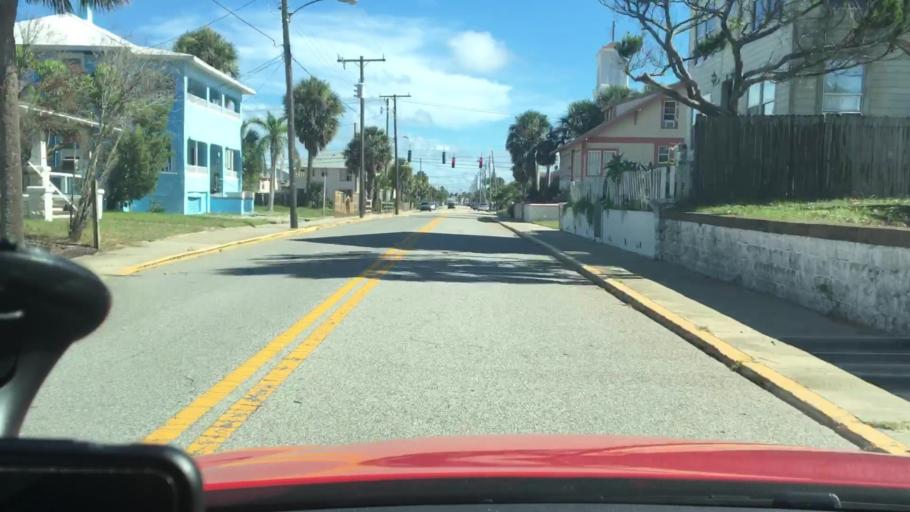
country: US
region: Florida
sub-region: Volusia County
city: Daytona Beach
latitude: 29.2254
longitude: -81.0091
